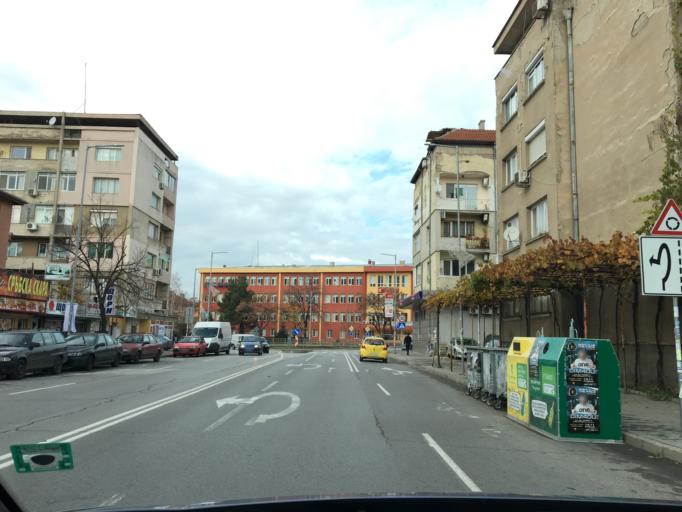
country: BG
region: Blagoevgrad
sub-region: Obshtina Blagoevgrad
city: Blagoevgrad
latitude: 42.0164
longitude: 23.0952
